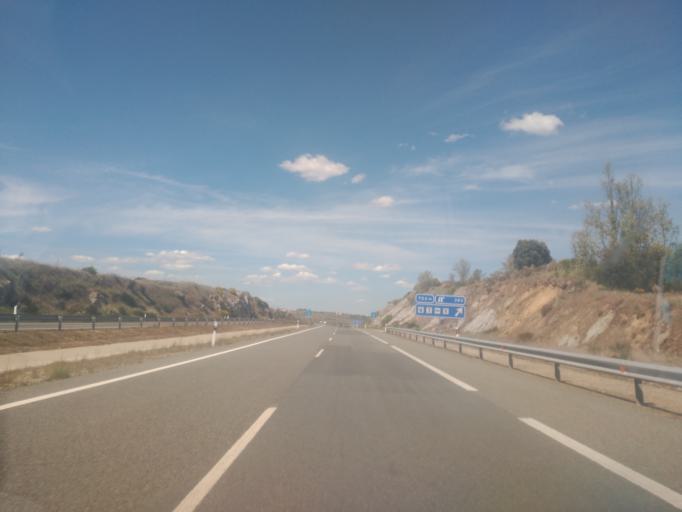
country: ES
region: Castille and Leon
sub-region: Provincia de Salamanca
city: Fuentes de Bejar
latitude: 40.5119
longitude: -5.6740
